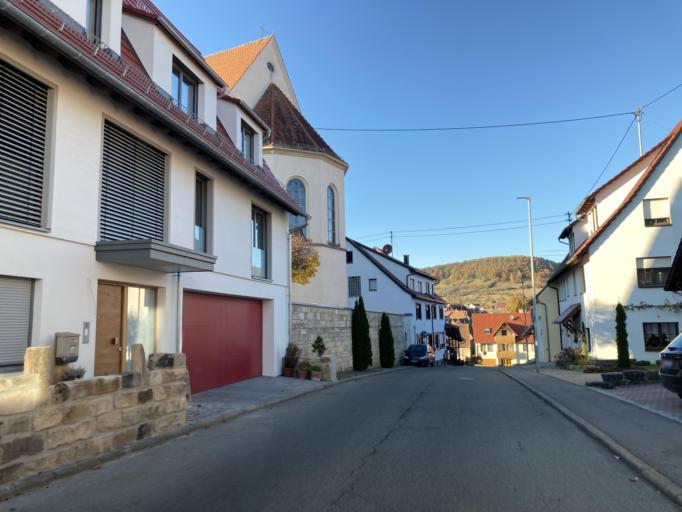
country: DE
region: Baden-Wuerttemberg
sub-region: Tuebingen Region
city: Rottenburg
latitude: 48.4353
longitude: 8.9348
